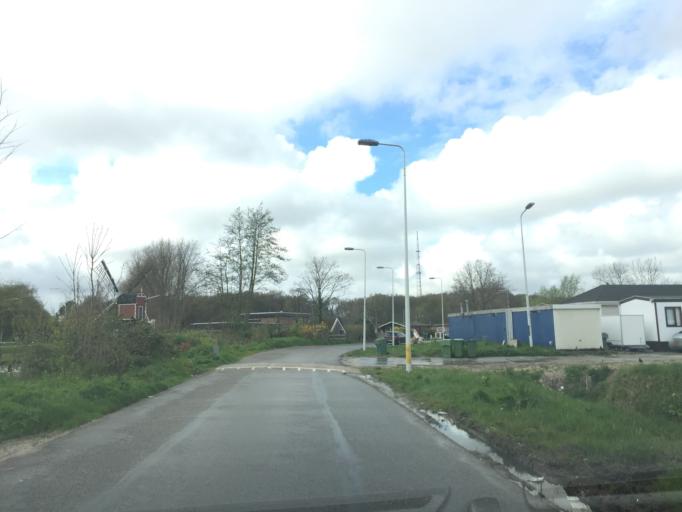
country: NL
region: South Holland
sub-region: Gemeente Leiden
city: Leiden
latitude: 52.1763
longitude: 4.4881
